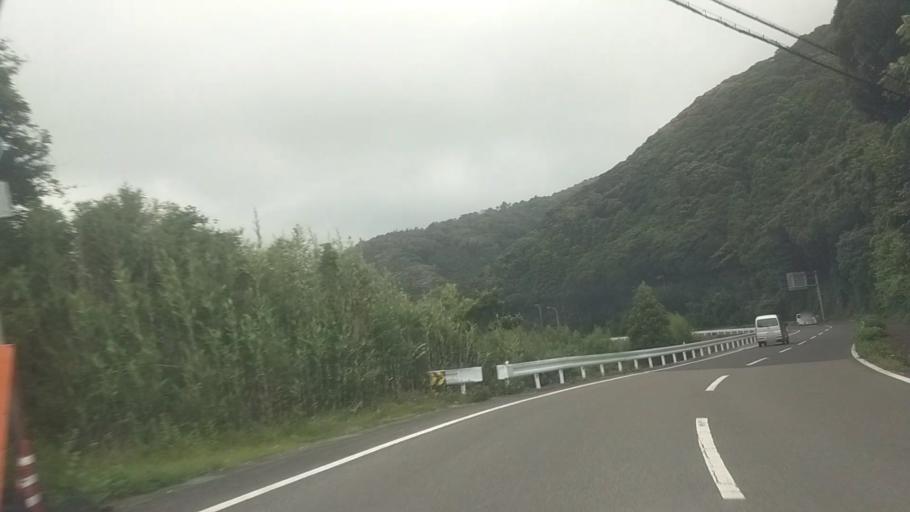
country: JP
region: Chiba
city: Kawaguchi
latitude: 35.1283
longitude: 140.1518
